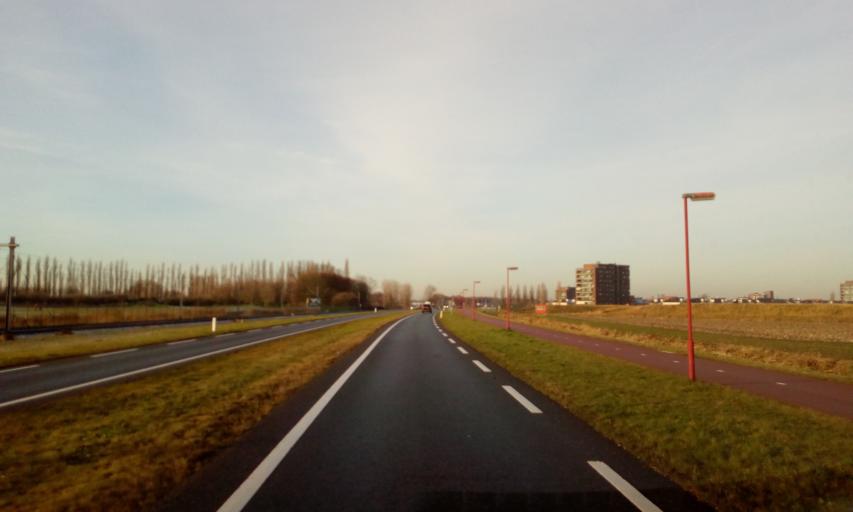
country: NL
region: South Holland
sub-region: Gemeente Pijnacker-Nootdorp
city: Pijnacker
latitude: 52.0575
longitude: 4.4280
